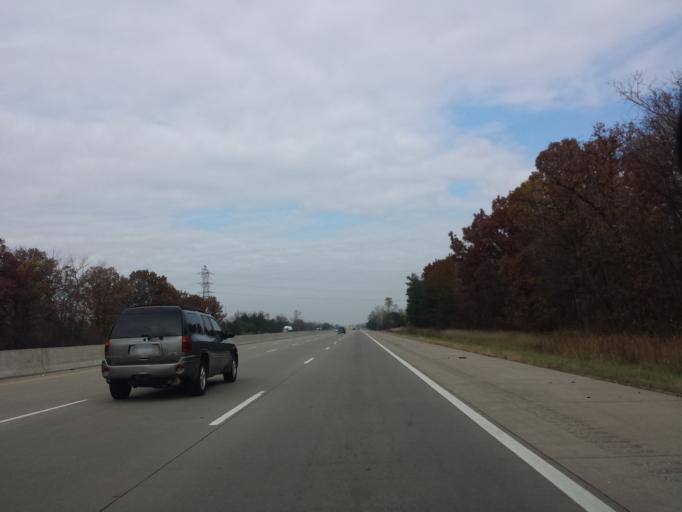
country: US
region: Michigan
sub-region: Saginaw County
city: Birch Run
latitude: 43.2110
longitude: -83.7688
